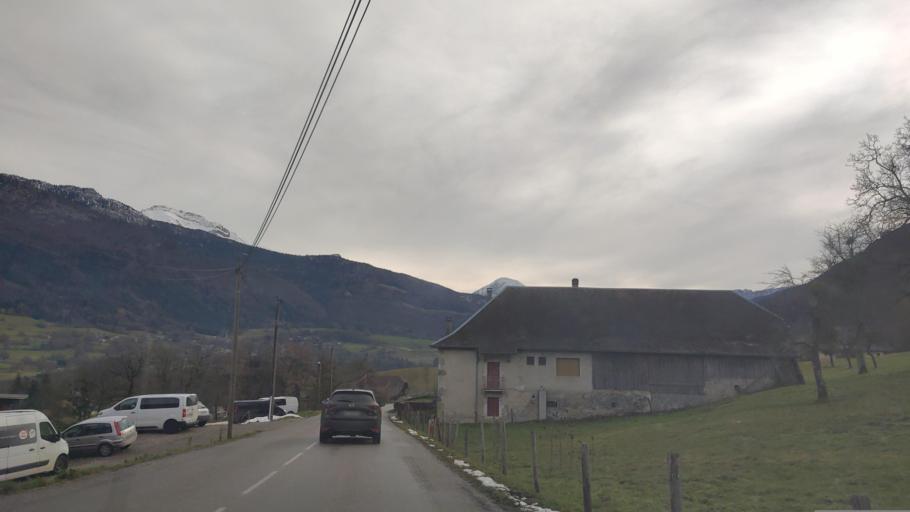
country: FR
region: Rhone-Alpes
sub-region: Departement de la Haute-Savoie
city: Gruffy
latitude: 45.7066
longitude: 6.1008
